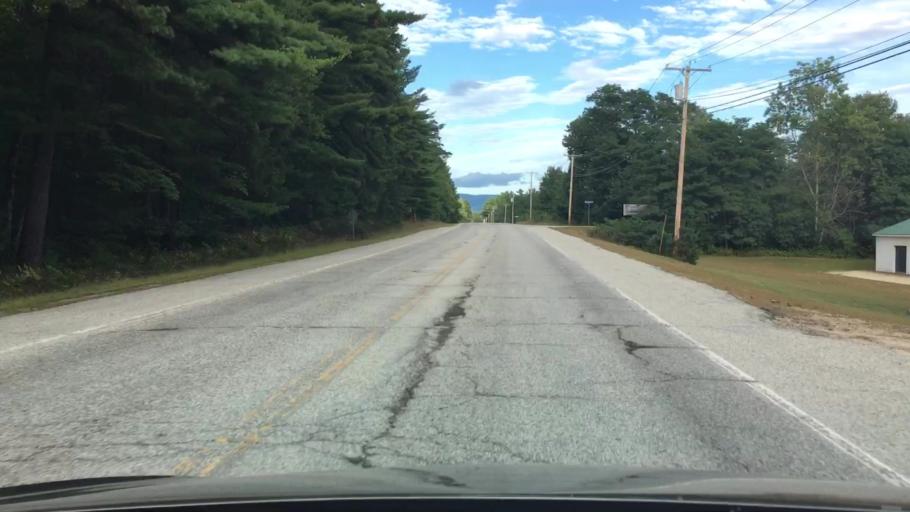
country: US
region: Maine
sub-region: Oxford County
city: Fryeburg
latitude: 44.0203
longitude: -70.9626
